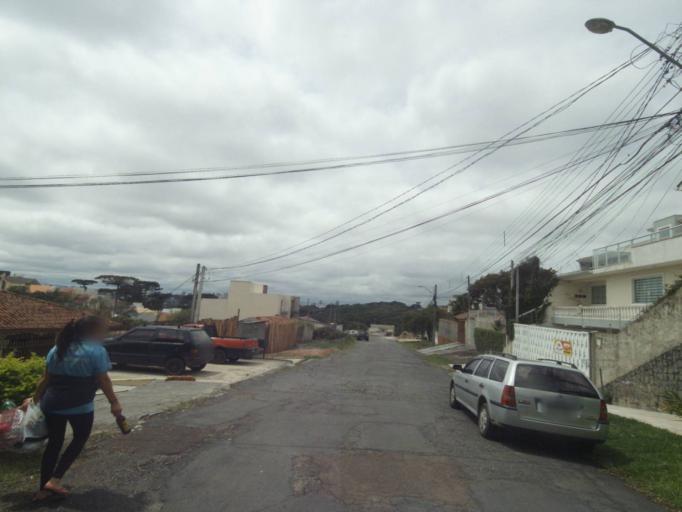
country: BR
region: Parana
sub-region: Curitiba
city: Curitiba
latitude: -25.3881
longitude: -49.2798
